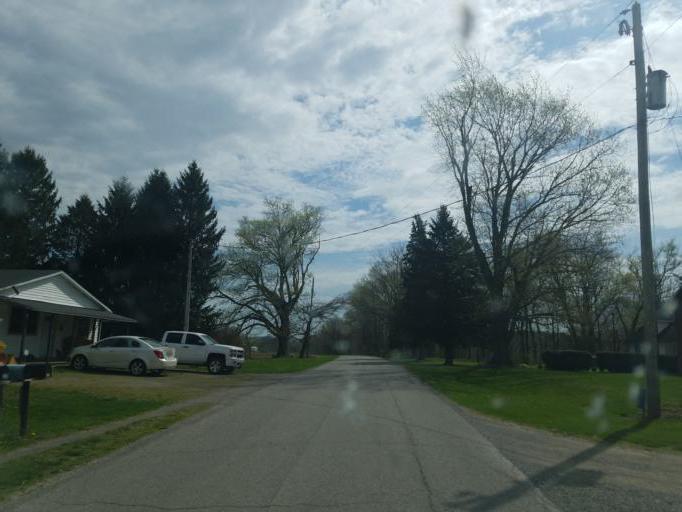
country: US
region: Ohio
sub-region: Crawford County
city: Bucyrus
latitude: 40.7902
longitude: -83.0317
